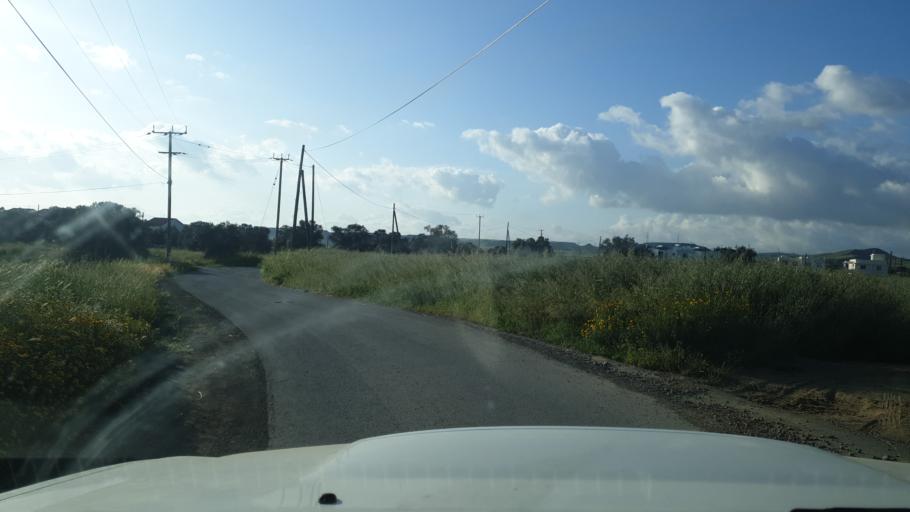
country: CY
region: Lefkosia
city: Tseri
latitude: 35.0623
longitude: 33.3282
